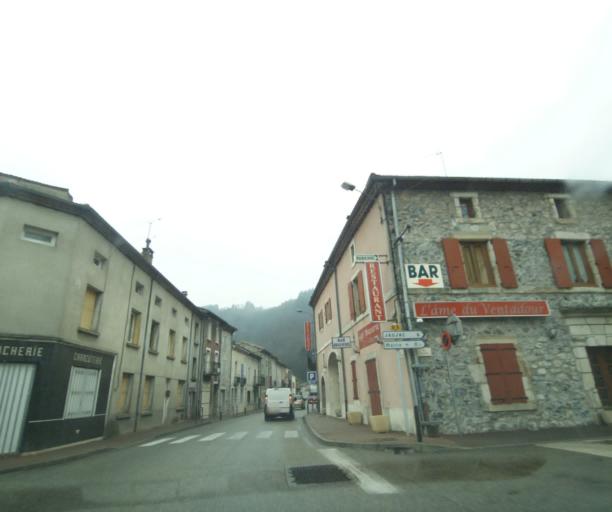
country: FR
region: Rhone-Alpes
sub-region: Departement de l'Ardeche
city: Jaujac
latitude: 44.6664
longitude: 4.2895
